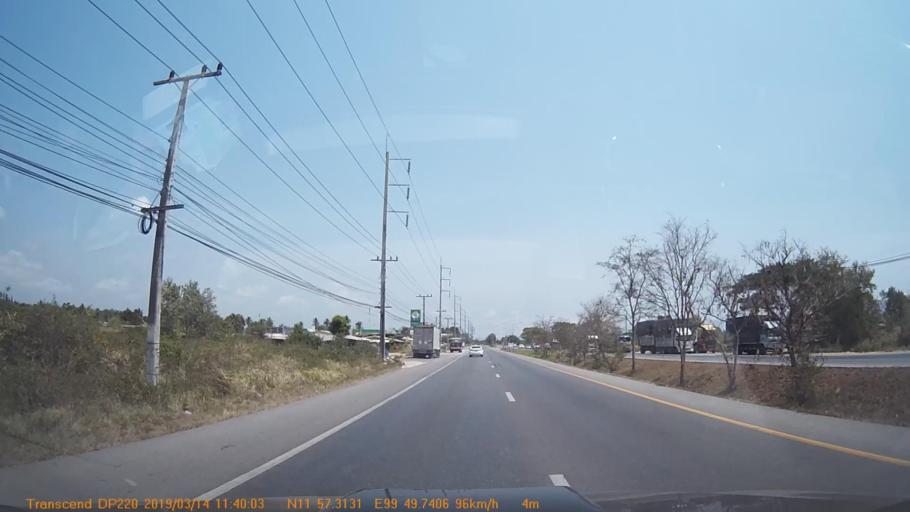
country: TH
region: Prachuap Khiri Khan
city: Kui Buri
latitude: 11.9556
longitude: 99.8292
